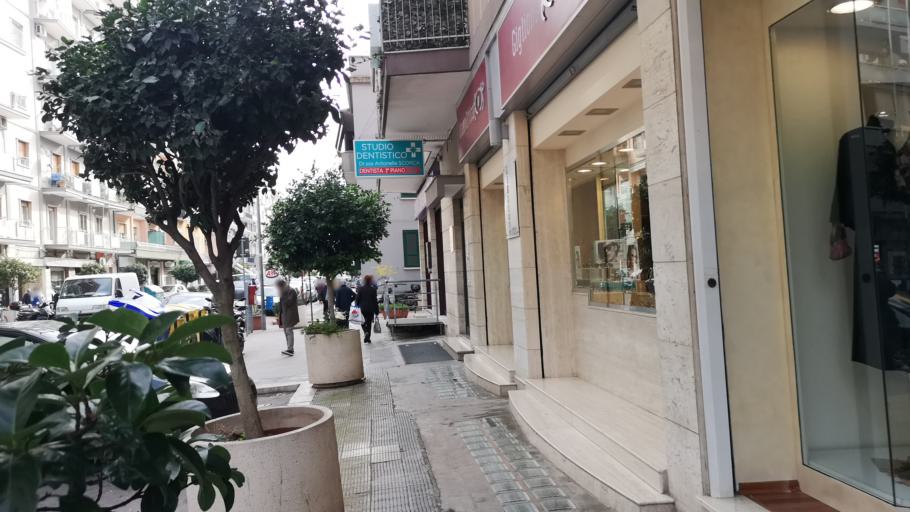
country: IT
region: Apulia
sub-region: Provincia di Bari
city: Bari
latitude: 41.1161
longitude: 16.8907
